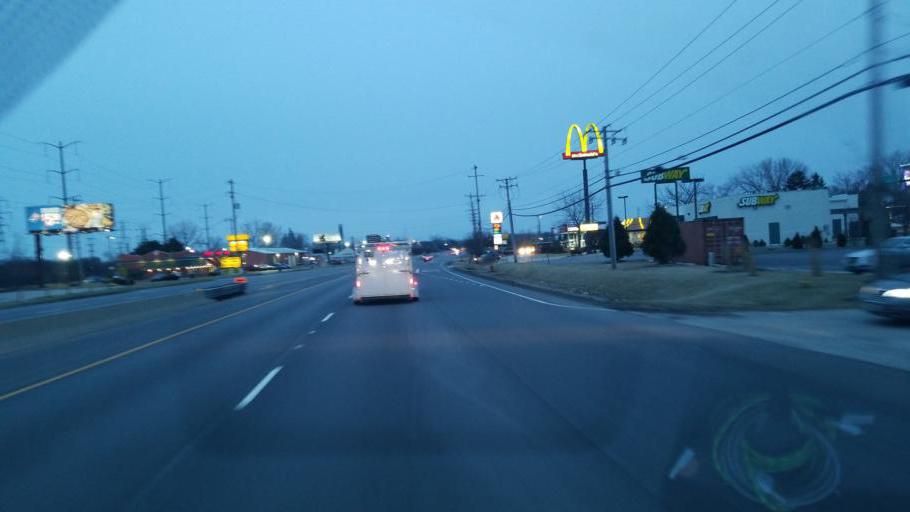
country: US
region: Illinois
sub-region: Lake County
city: Knollwood
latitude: 42.3052
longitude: -87.8760
